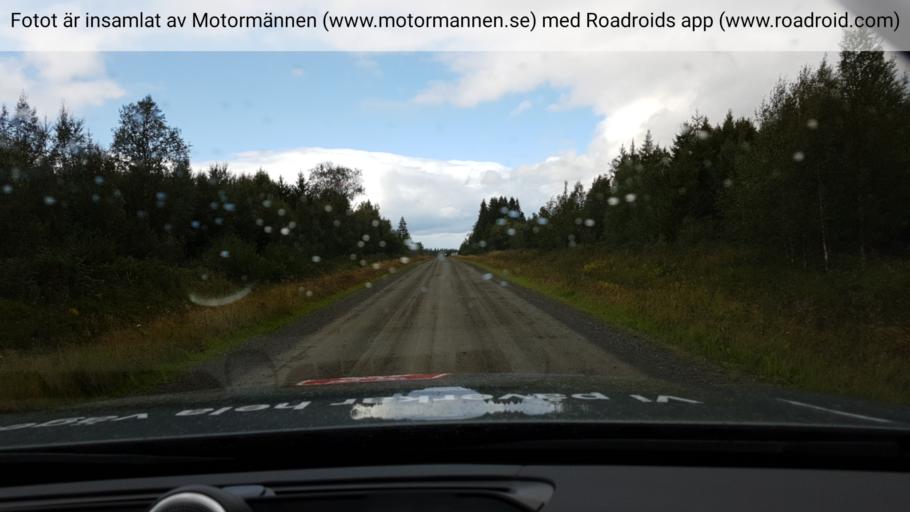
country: SE
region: Jaemtland
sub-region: OEstersunds Kommun
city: Lit
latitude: 63.6776
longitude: 14.8674
